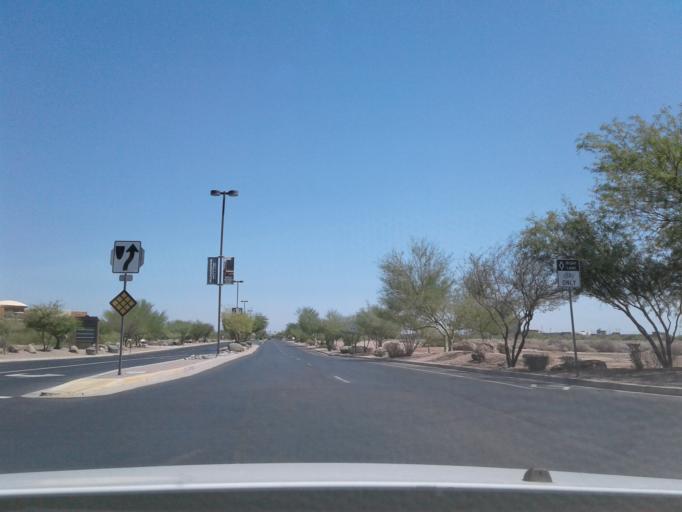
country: US
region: Arizona
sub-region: Maricopa County
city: Guadalupe
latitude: 33.2722
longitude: -111.9785
